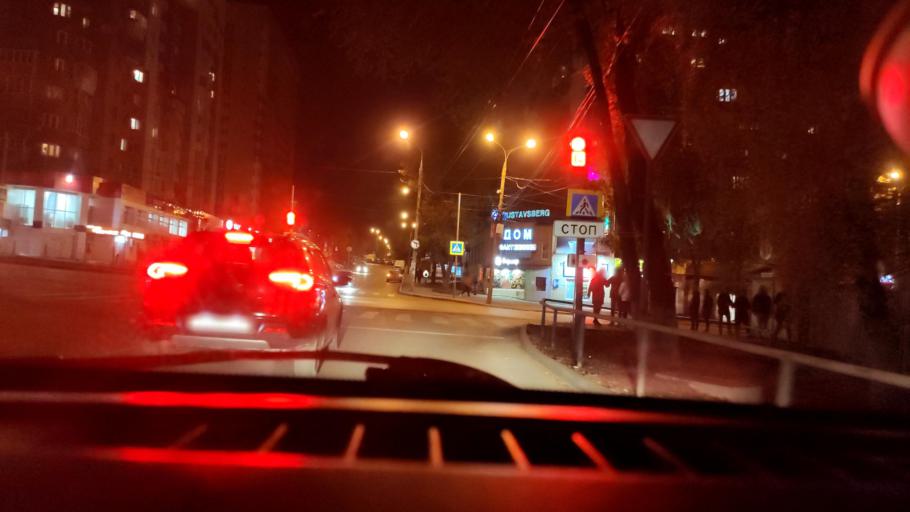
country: RU
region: Samara
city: Samara
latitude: 53.2062
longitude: 50.2212
